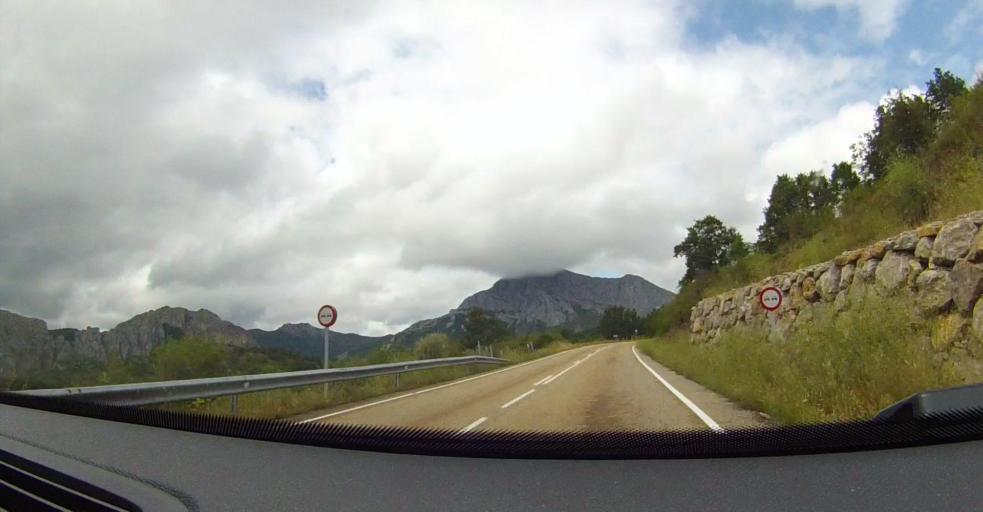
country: ES
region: Castille and Leon
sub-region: Provincia de Leon
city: Puebla de Lillo
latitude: 42.9633
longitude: -5.2553
